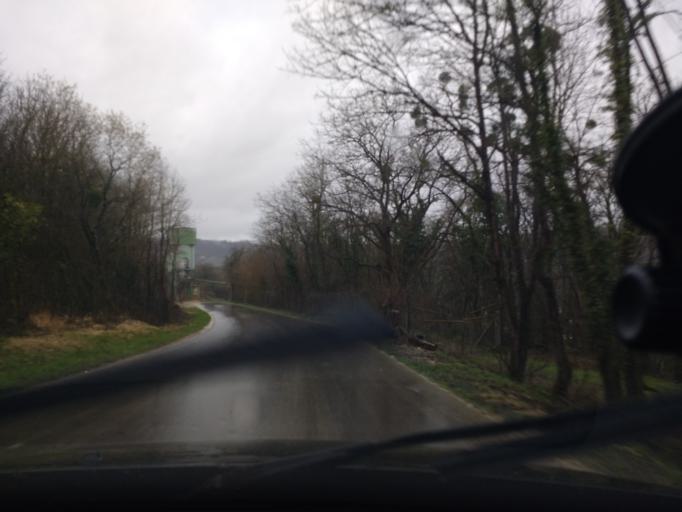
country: LU
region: Grevenmacher
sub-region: Canton de Grevenmacher
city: Grevenmacher
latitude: 49.6701
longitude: 6.4426
